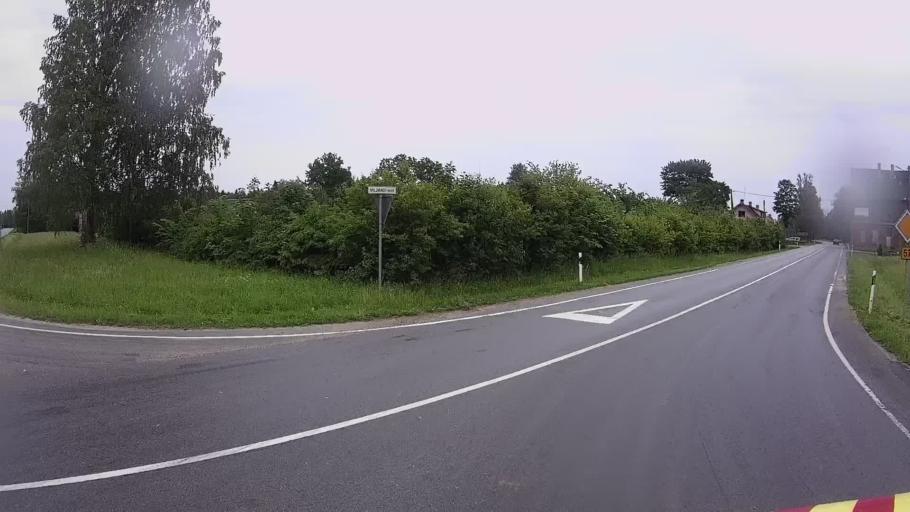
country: EE
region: Paernumaa
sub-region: Vaendra vald (alev)
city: Vandra
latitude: 58.6576
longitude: 25.0501
